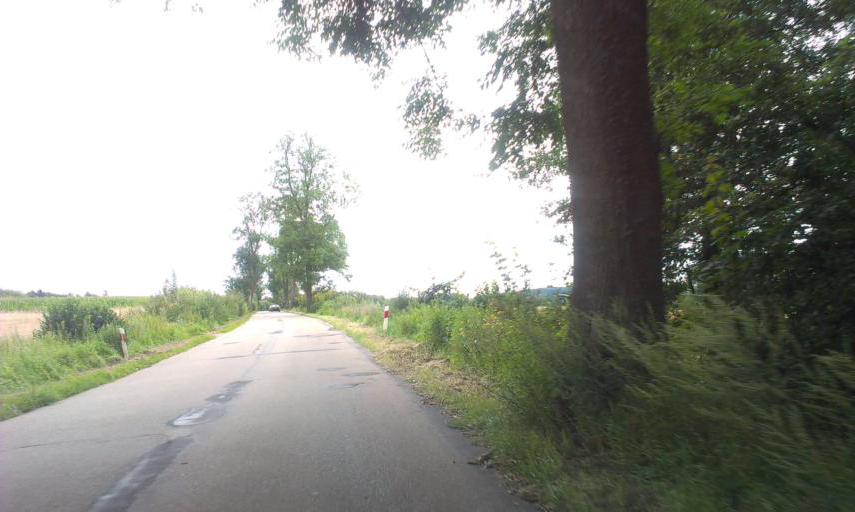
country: PL
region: West Pomeranian Voivodeship
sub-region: Powiat szczecinecki
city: Barwice
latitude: 53.7207
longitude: 16.3547
